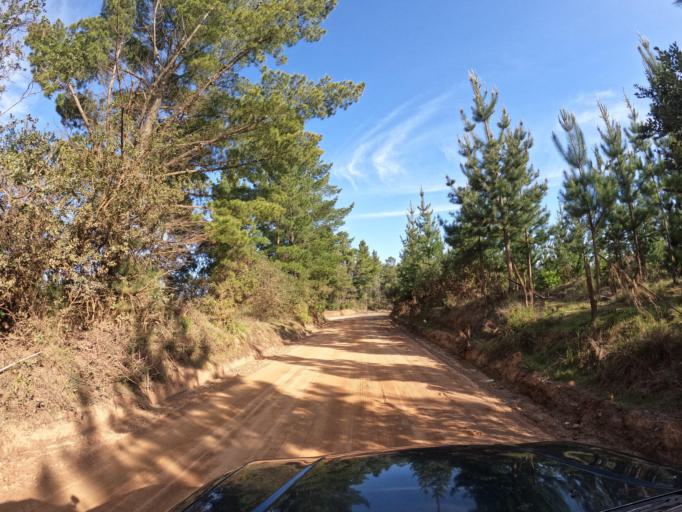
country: CL
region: Biobio
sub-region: Provincia de Biobio
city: La Laja
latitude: -37.1142
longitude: -72.7390
